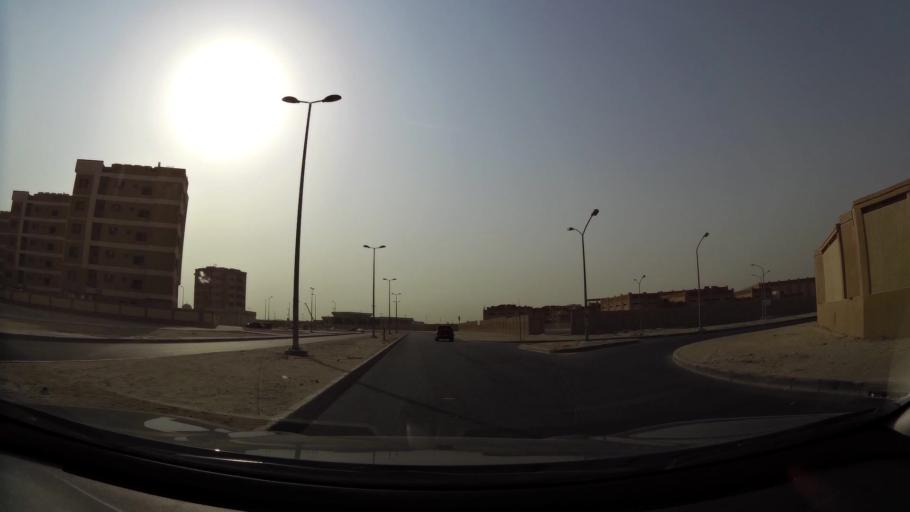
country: KW
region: Al Asimah
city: Ar Rabiyah
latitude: 29.3237
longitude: 47.8166
